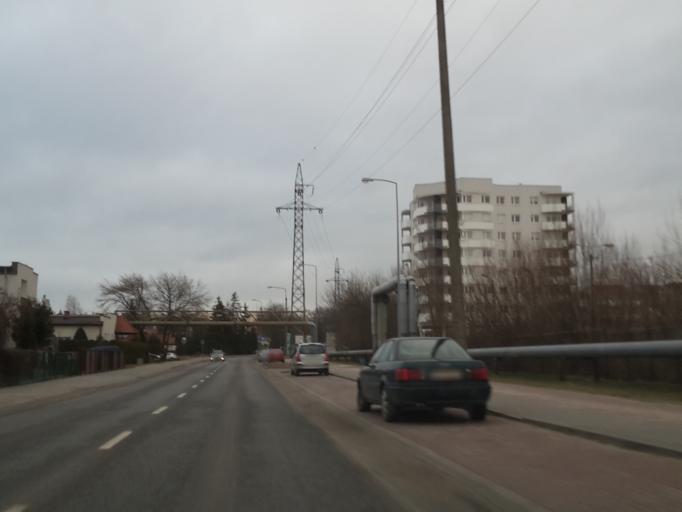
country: PL
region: Warmian-Masurian Voivodeship
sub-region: Powiat elblaski
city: Elblag
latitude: 54.1800
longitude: 19.4225
